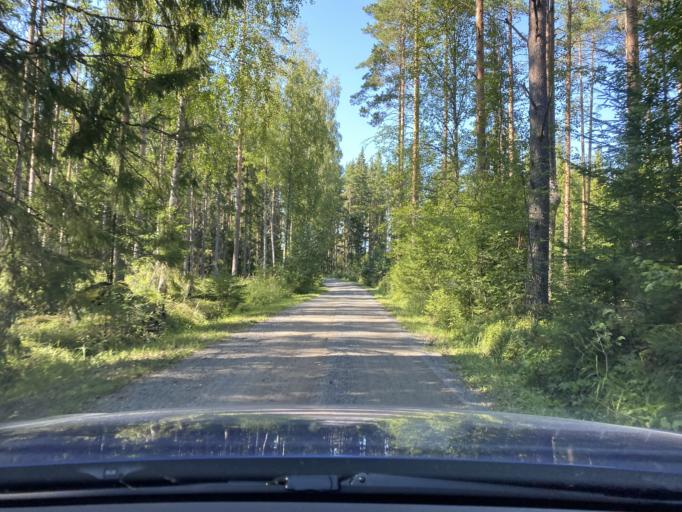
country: FI
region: Satakunta
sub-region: Rauma
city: Kiukainen
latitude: 61.1426
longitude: 22.0241
